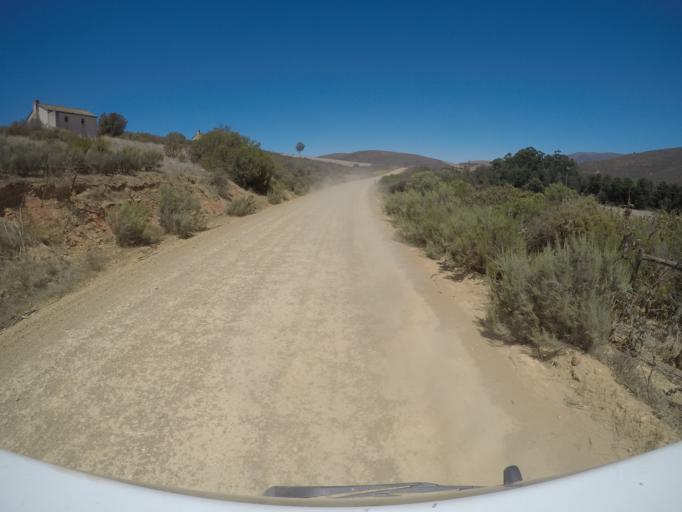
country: ZA
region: Western Cape
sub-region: Overberg District Municipality
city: Caledon
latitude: -34.1391
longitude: 19.2481
